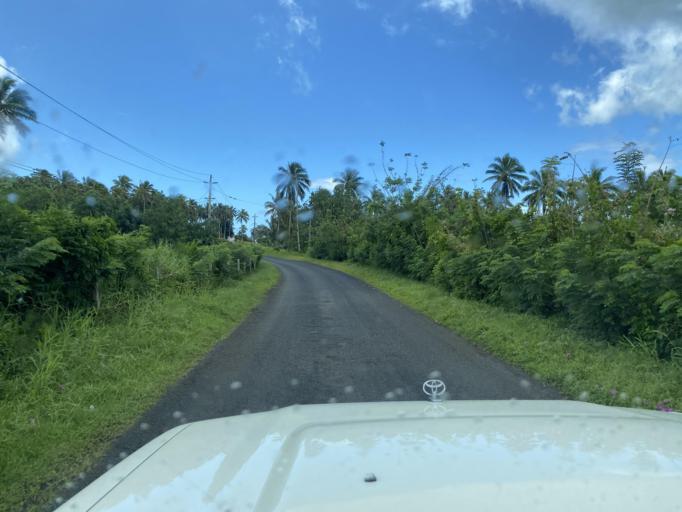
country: WS
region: Va`a-o-Fonoti
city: Samamea
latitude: -13.9817
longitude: -171.5878
